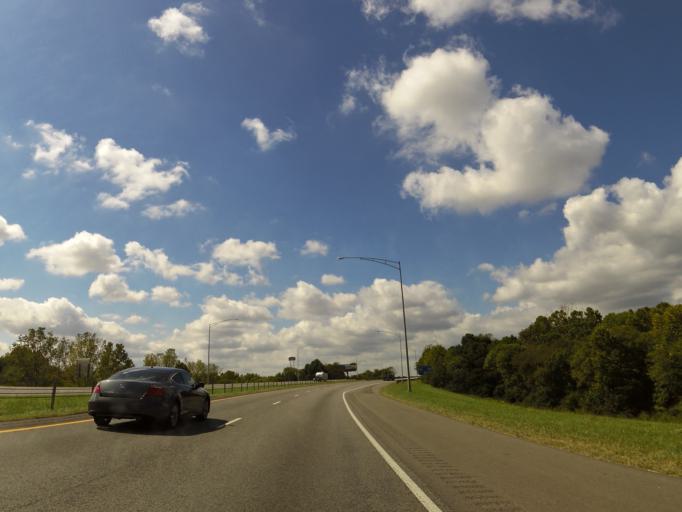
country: US
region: Alabama
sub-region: Jefferson County
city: Bessemer
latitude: 33.4153
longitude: -86.9643
